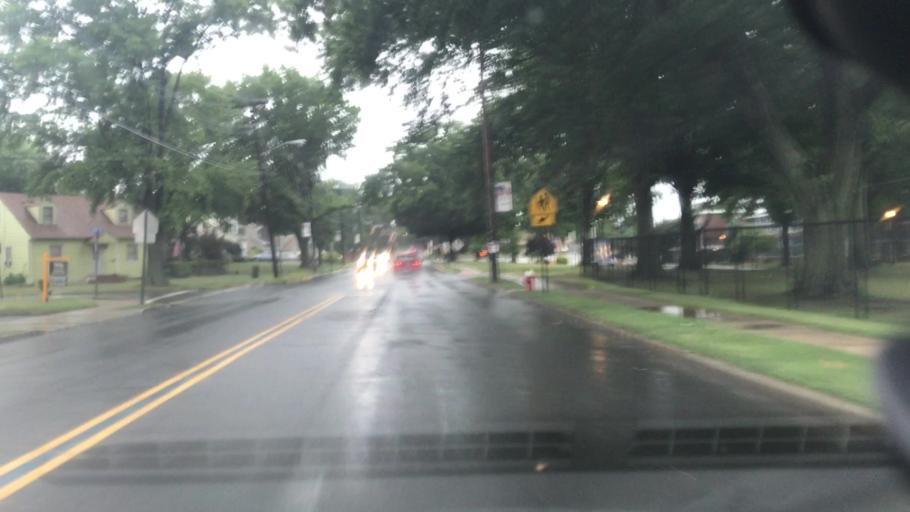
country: US
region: New Jersey
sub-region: Union County
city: Clark
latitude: 40.6241
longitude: -74.3133
